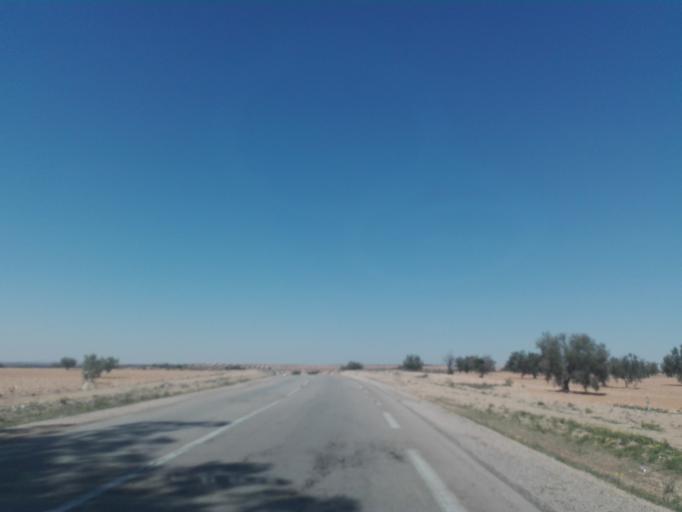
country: TN
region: Safaqis
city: Bi'r `Ali Bin Khalifah
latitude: 34.7589
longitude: 10.3028
